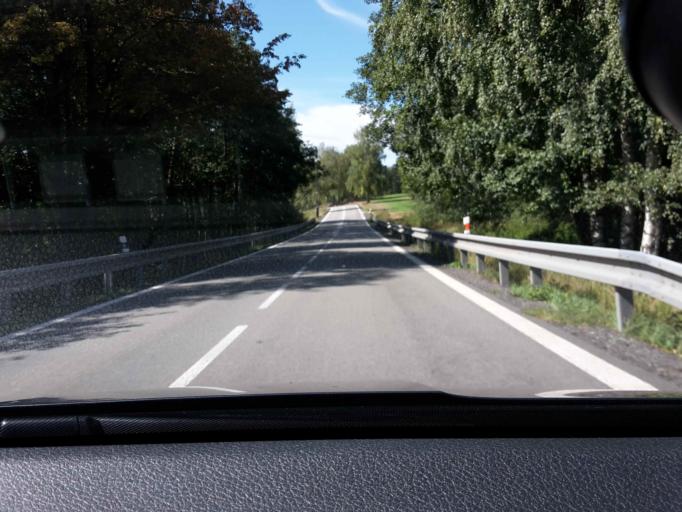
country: CZ
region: Jihocesky
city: Strmilov
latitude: 49.1659
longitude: 15.2237
